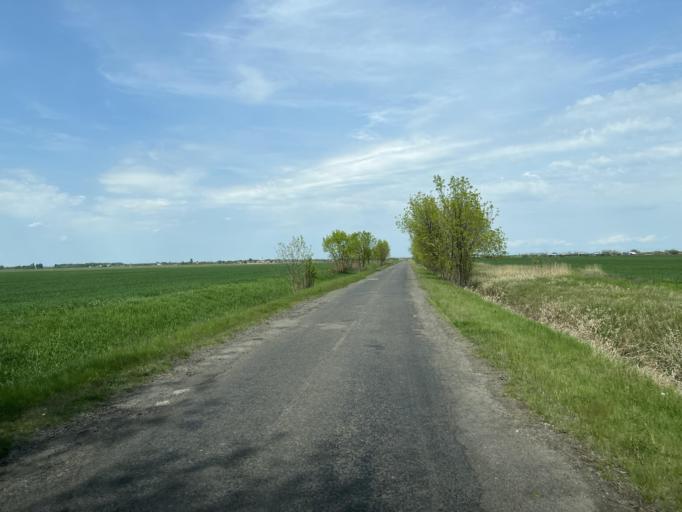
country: HU
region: Pest
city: Tapiogyorgye
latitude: 47.3100
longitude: 19.9738
